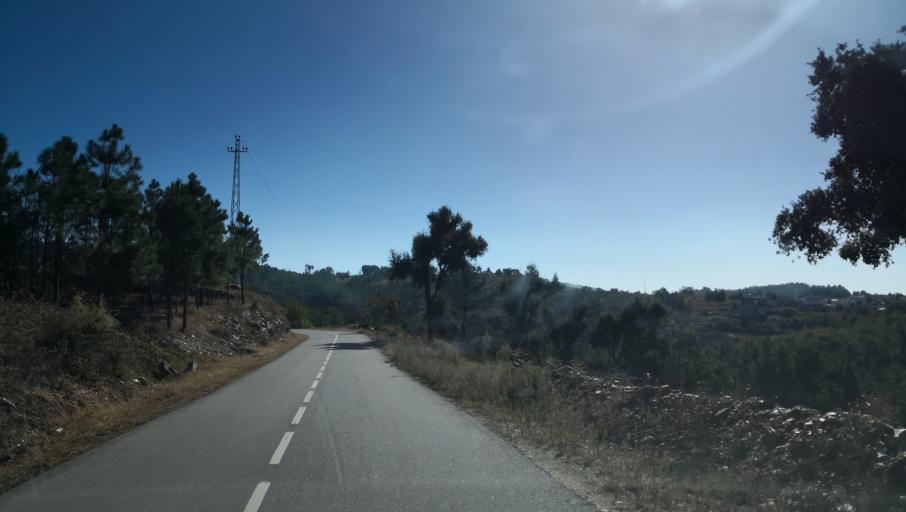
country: PT
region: Vila Real
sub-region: Sabrosa
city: Vilela
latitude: 41.2332
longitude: -7.6389
